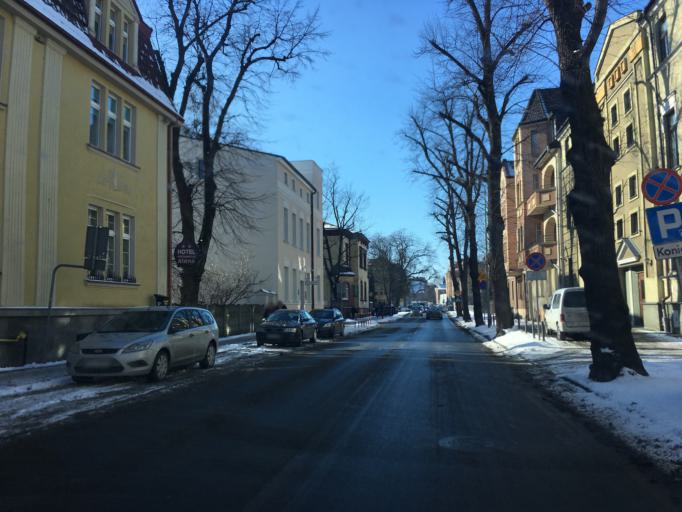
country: PL
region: Pomeranian Voivodeship
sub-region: Slupsk
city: Slupsk
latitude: 54.4703
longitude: 17.0332
